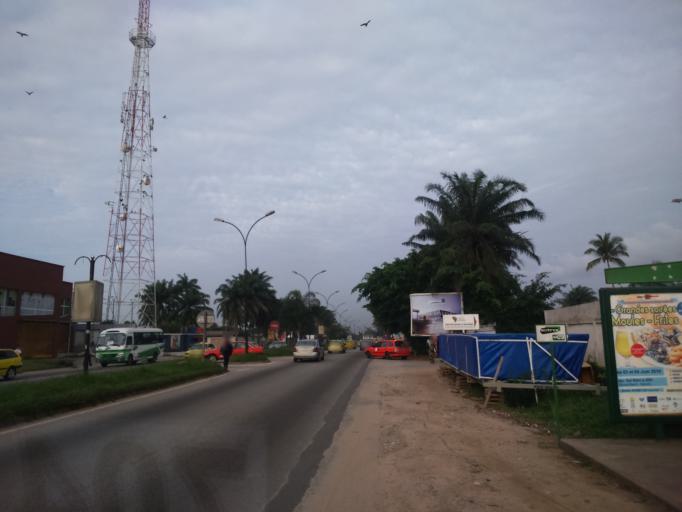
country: CI
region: Lagunes
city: Abidjan
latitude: 5.3601
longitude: -3.9988
